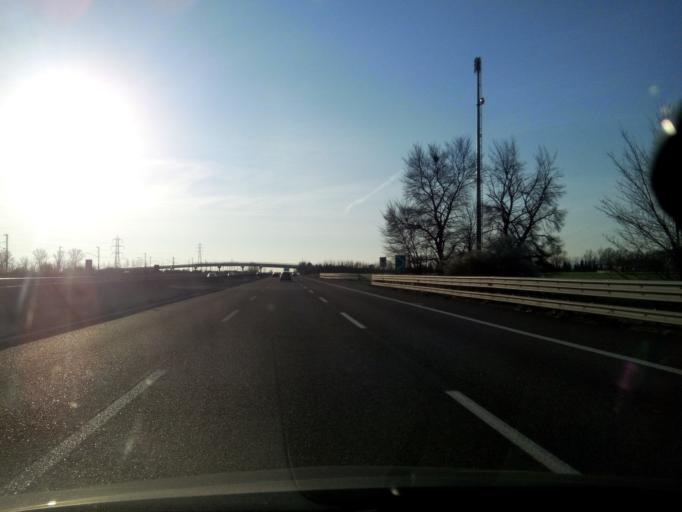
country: IT
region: Emilia-Romagna
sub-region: Provincia di Piacenza
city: Pontenure
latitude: 44.9992
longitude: 9.8167
